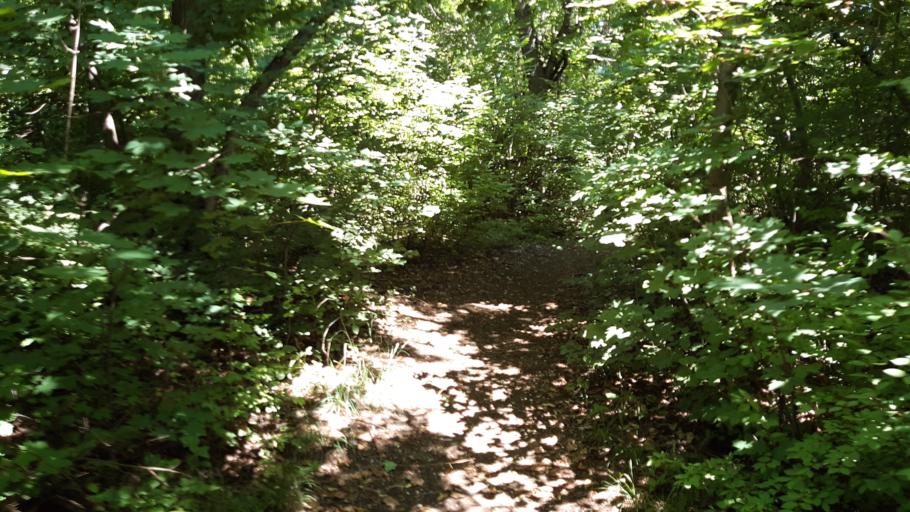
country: HU
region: Pest
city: Budaors
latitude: 47.4798
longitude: 18.9676
